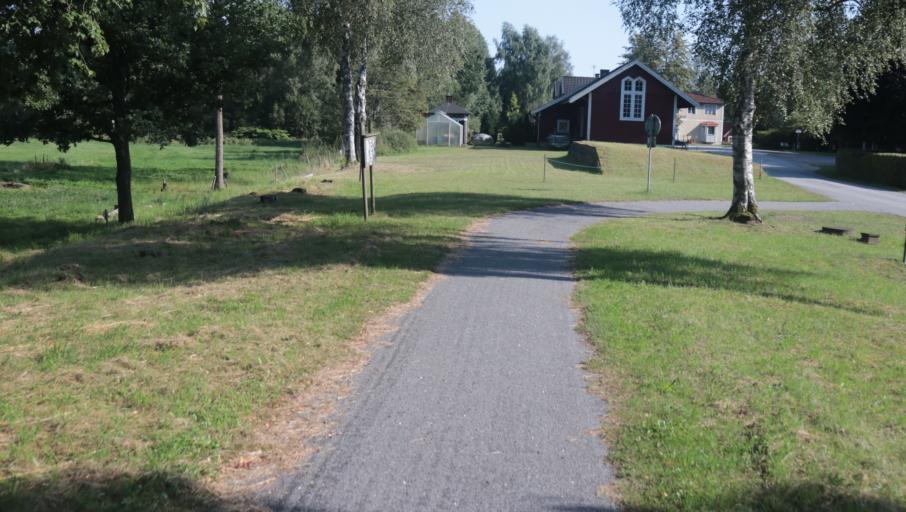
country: SE
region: Blekinge
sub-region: Karlshamns Kommun
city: Svangsta
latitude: 56.3892
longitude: 14.6748
